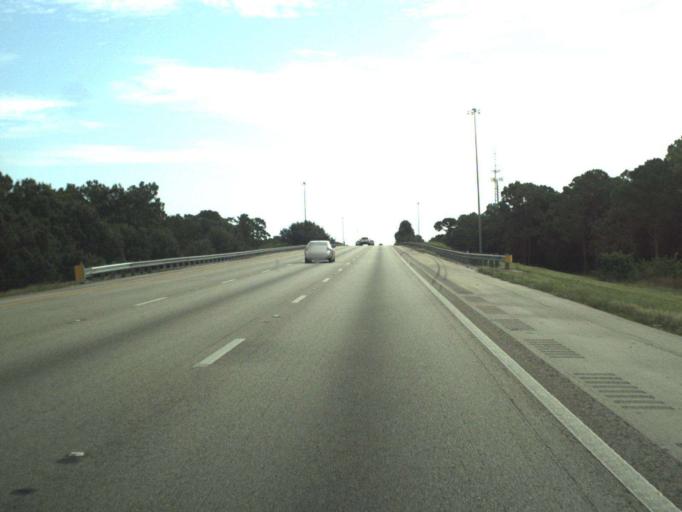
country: US
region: Florida
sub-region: Saint Lucie County
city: Fort Pierce South
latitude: 27.3712
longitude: -80.4102
